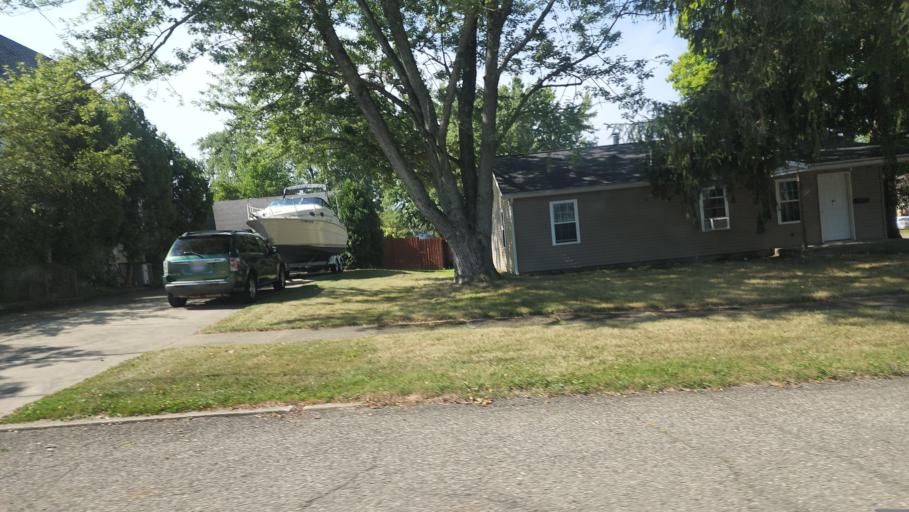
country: US
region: Ohio
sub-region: Trumbull County
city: Niles
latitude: 41.1877
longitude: -80.7574
